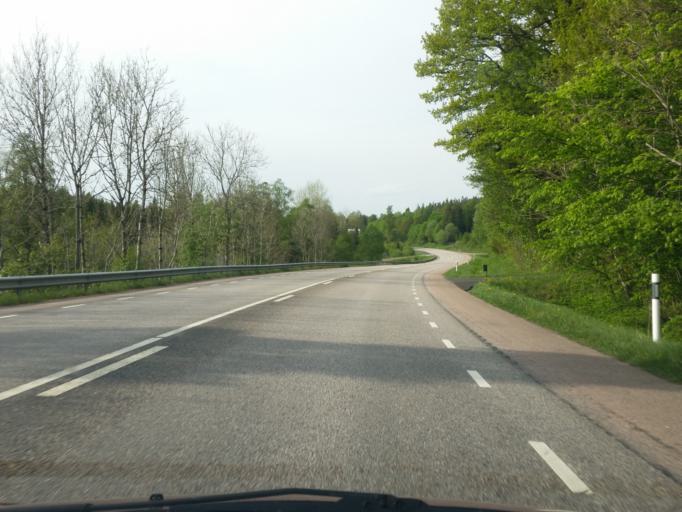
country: SE
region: Vaestra Goetaland
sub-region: Ulricehamns Kommun
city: Ulricehamn
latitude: 57.8066
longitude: 13.2978
